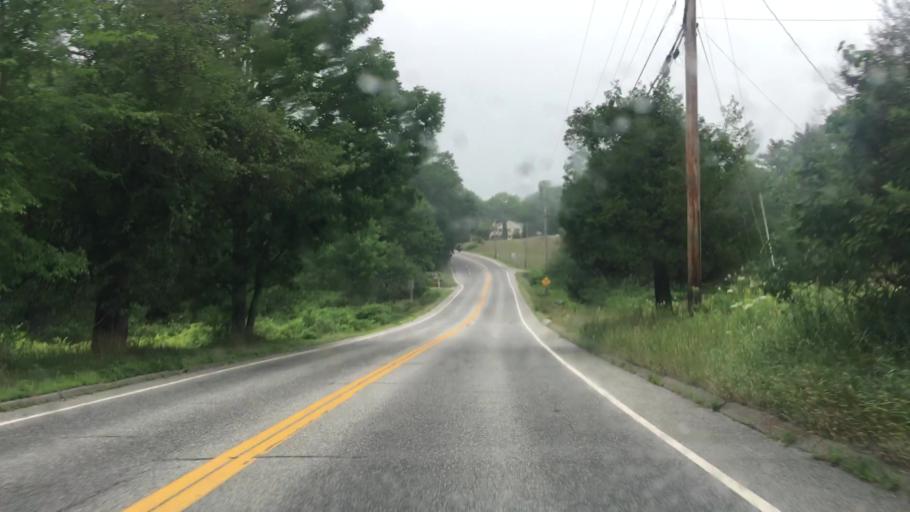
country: US
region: Maine
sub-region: Lincoln County
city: Edgecomb
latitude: 43.9521
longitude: -69.6295
